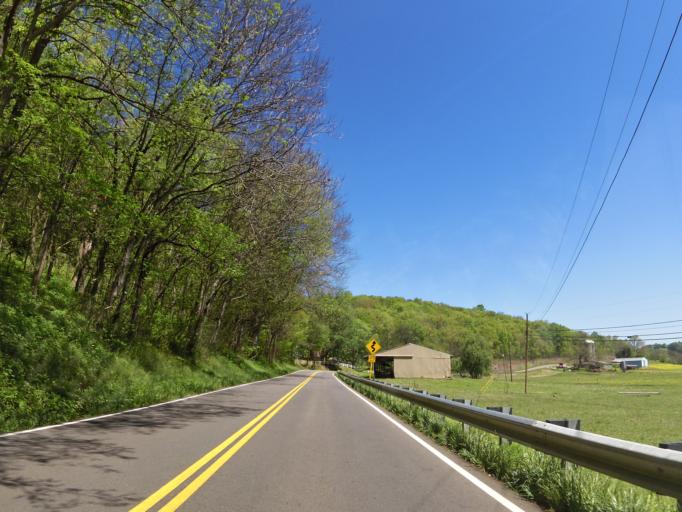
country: US
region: Tennessee
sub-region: Greene County
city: Mosheim
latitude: 36.0826
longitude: -82.9580
